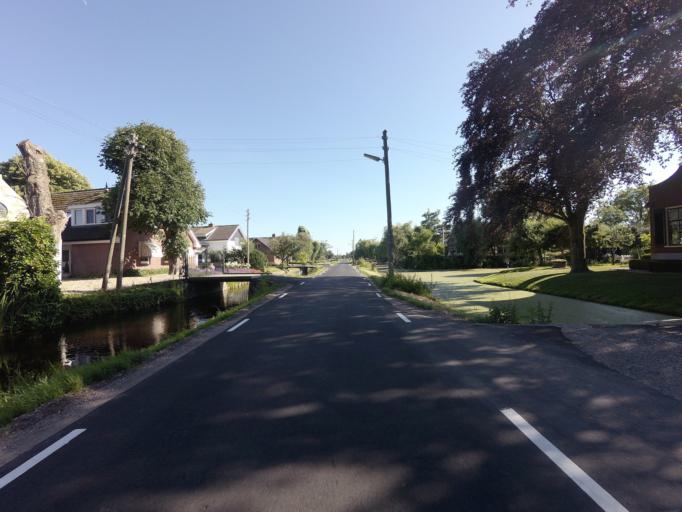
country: NL
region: South Holland
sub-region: Gemeente Waddinxveen
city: Vondelwijk
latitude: 52.0550
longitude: 4.6808
